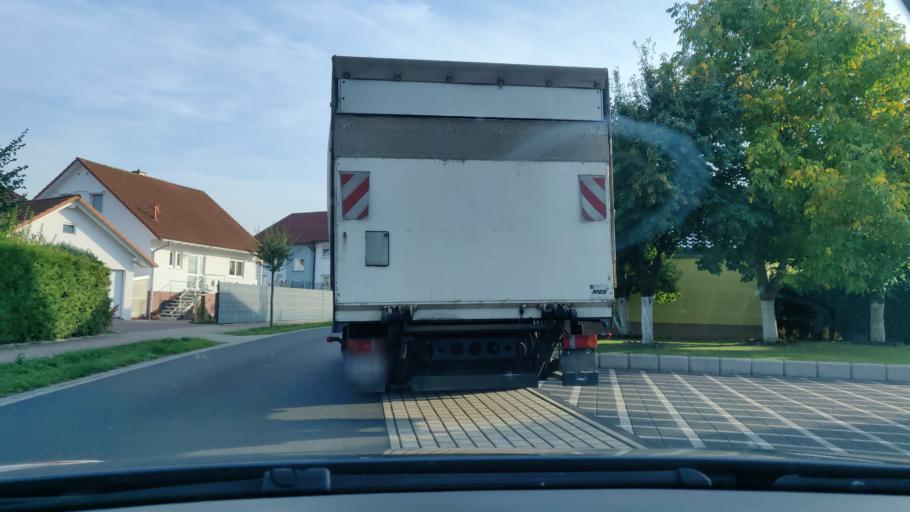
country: DE
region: Hesse
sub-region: Regierungsbezirk Kassel
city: Wabern
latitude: 51.0974
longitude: 9.3427
